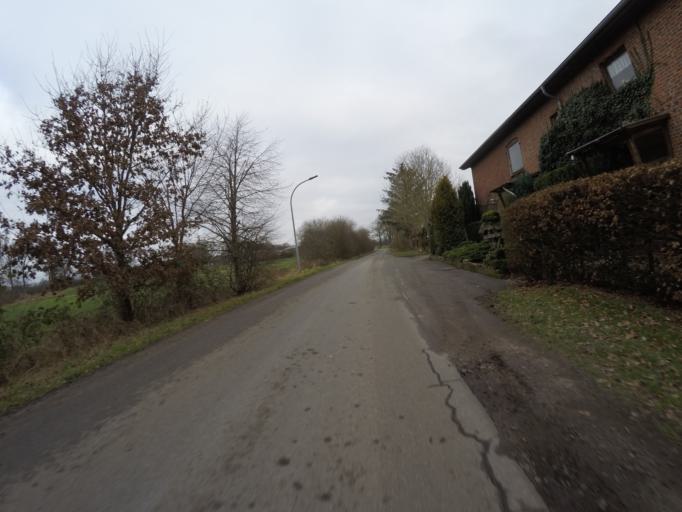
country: DE
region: Schleswig-Holstein
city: Langeln
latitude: 53.7958
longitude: 9.8649
